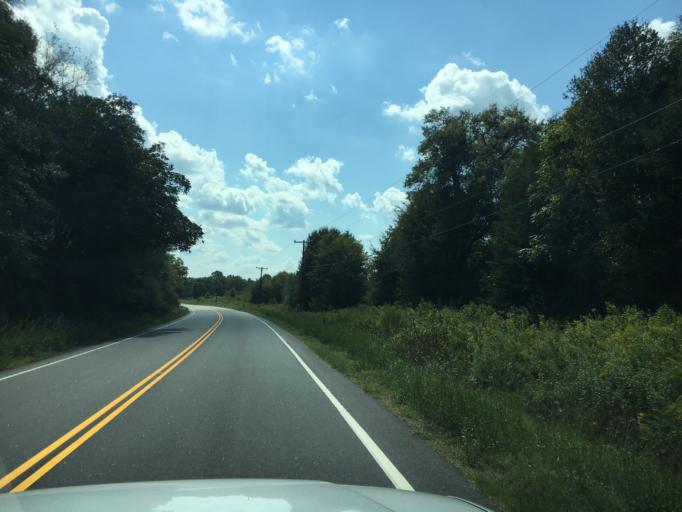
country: US
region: South Carolina
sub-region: Spartanburg County
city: Woodruff
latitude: 34.6678
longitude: -82.0837
